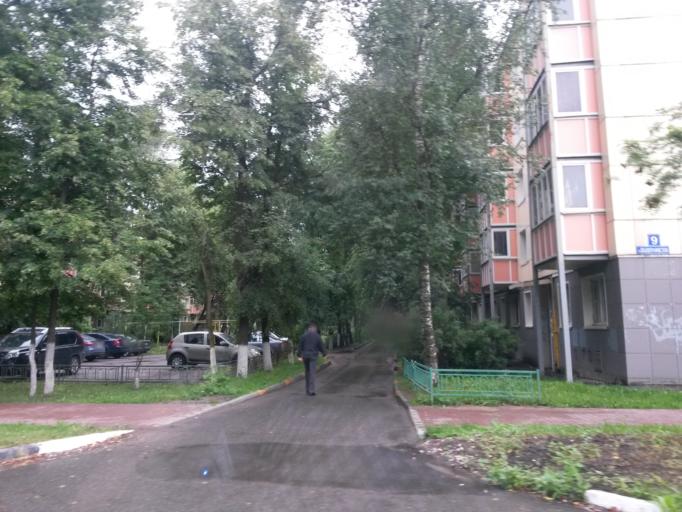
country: RU
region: Moskovskaya
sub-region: Chekhovskiy Rayon
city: Chekhov
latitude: 55.1556
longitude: 37.4714
